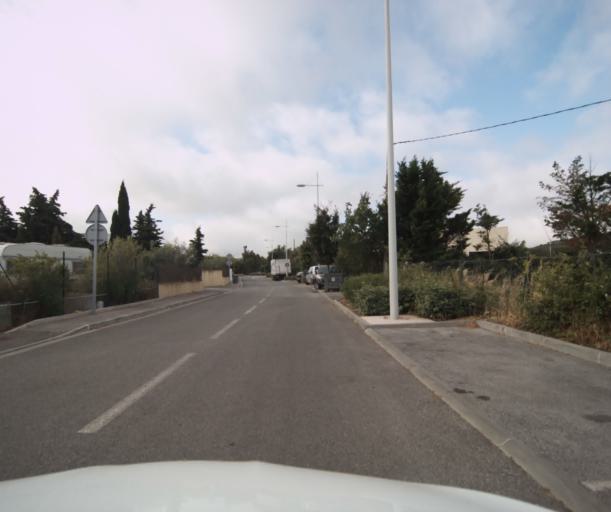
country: FR
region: Provence-Alpes-Cote d'Azur
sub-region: Departement du Var
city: Ollioules
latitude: 43.1186
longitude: 5.8419
